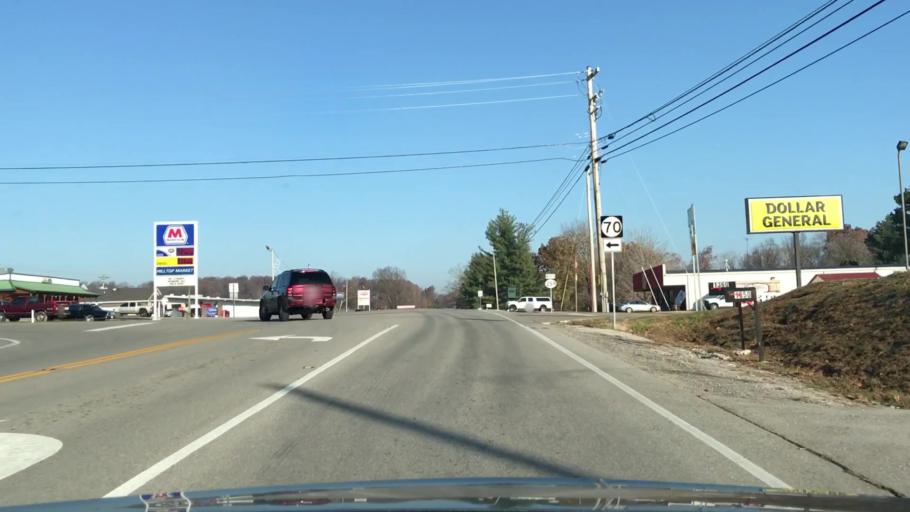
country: US
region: Kentucky
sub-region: Edmonson County
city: Brownsville
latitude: 37.2076
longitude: -86.2843
